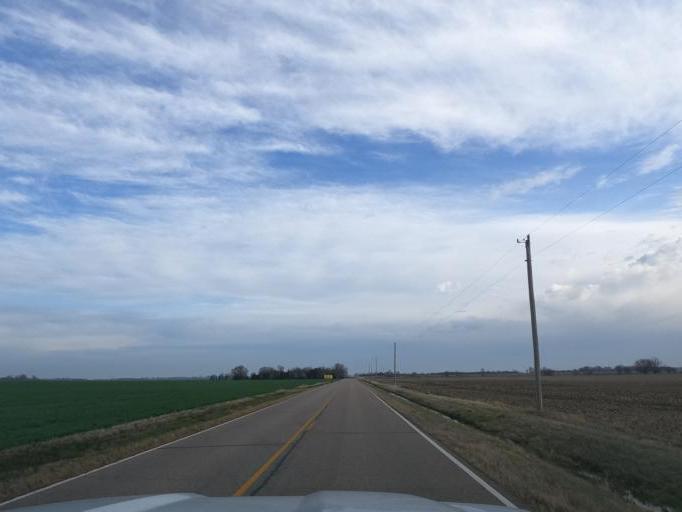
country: US
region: Kansas
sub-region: Reno County
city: Nickerson
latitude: 38.0473
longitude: -98.1792
